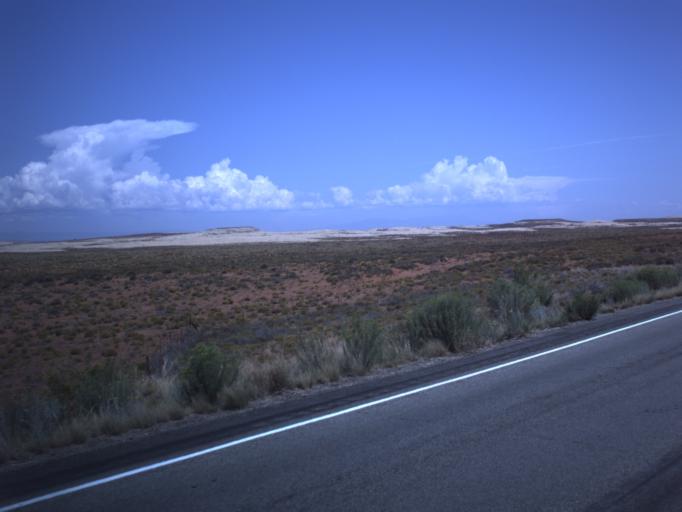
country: US
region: Utah
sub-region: San Juan County
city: Blanding
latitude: 37.0229
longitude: -109.6042
